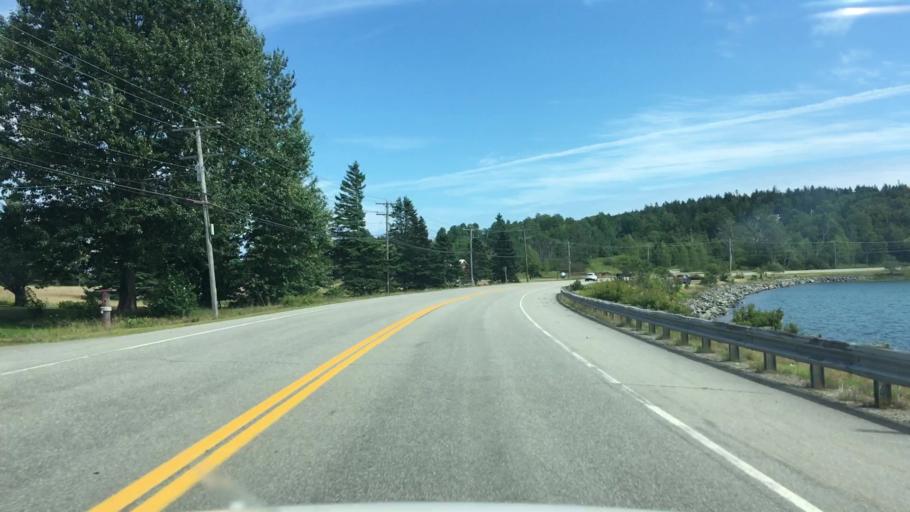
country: US
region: Maine
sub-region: Washington County
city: Eastport
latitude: 44.9253
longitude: -67.0179
